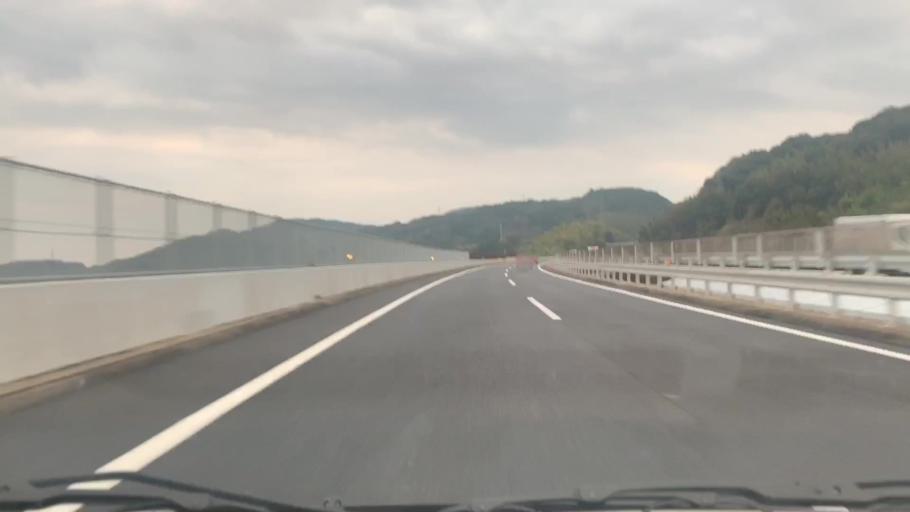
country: JP
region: Nagasaki
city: Omura
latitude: 32.8889
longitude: 129.9916
